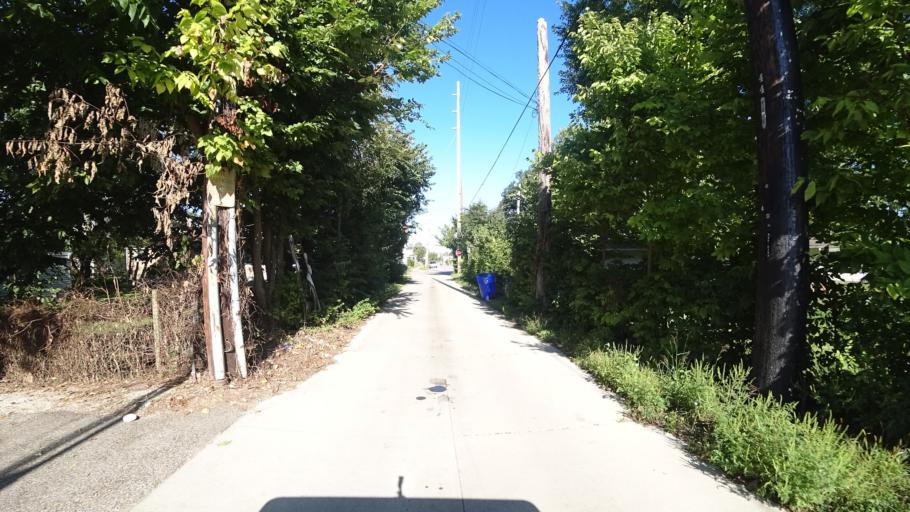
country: US
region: Ohio
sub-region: Butler County
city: Hamilton
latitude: 39.4004
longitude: -84.5461
